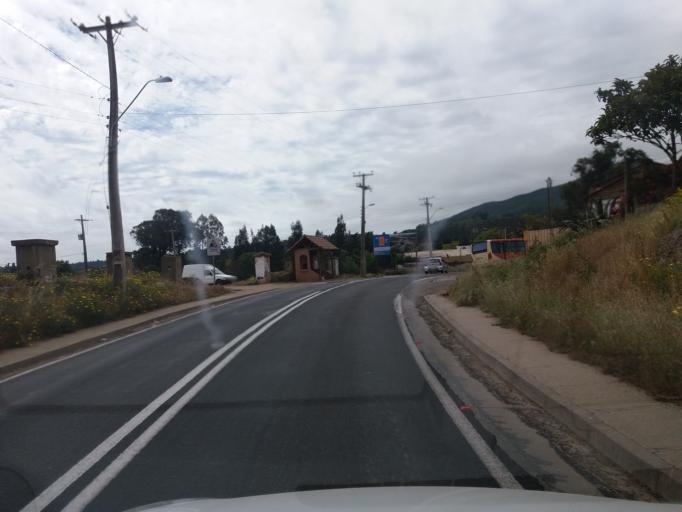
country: CL
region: Valparaiso
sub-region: Provincia de Marga Marga
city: Quilpue
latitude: -32.9219
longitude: -71.4436
